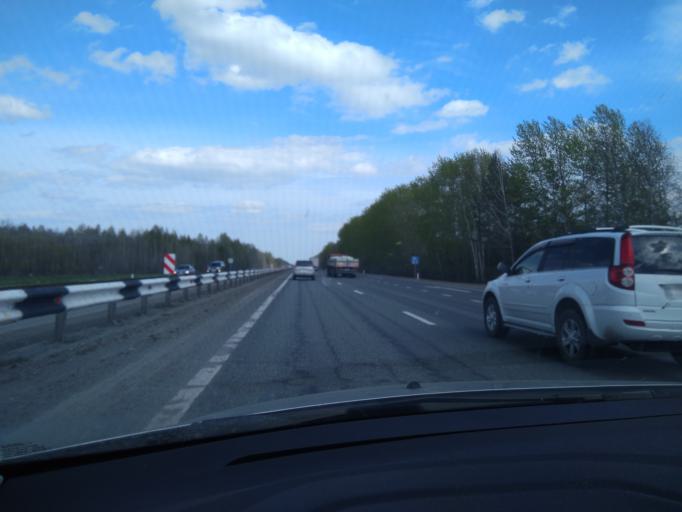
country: RU
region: Tjumen
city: Moskovskiy
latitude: 57.1058
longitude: 65.3497
